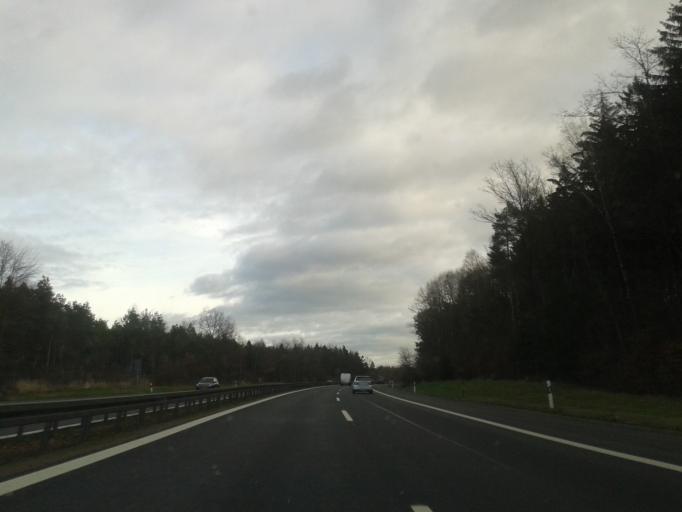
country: DE
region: Saxony
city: Grossrohrsdorf
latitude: 51.1588
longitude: 14.0244
